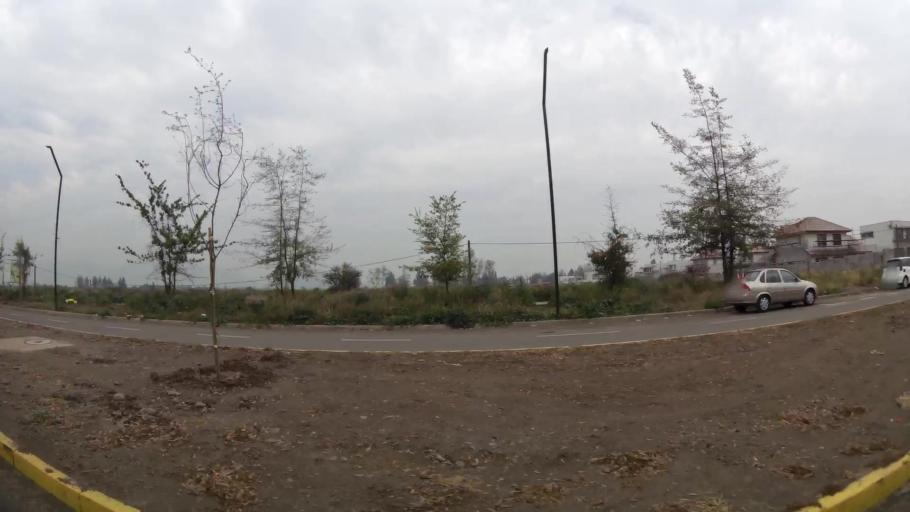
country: CL
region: Santiago Metropolitan
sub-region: Provincia de Chacabuco
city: Chicureo Abajo
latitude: -33.2176
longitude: -70.6676
